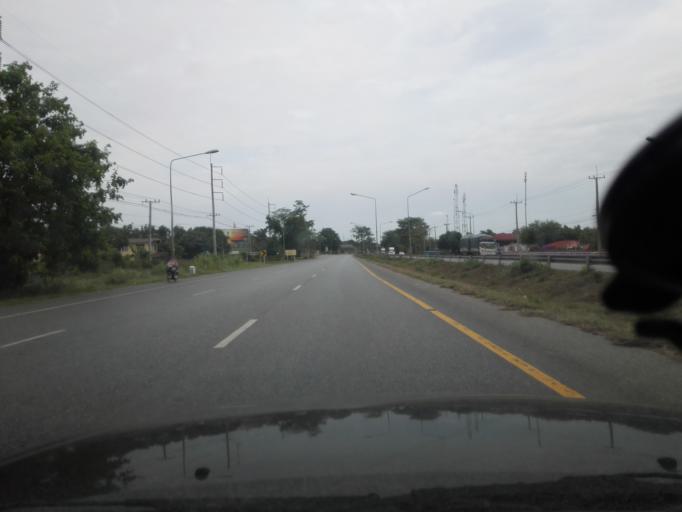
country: TH
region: Kamphaeng Phet
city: Khlong Khlung
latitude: 16.0999
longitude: 99.7207
